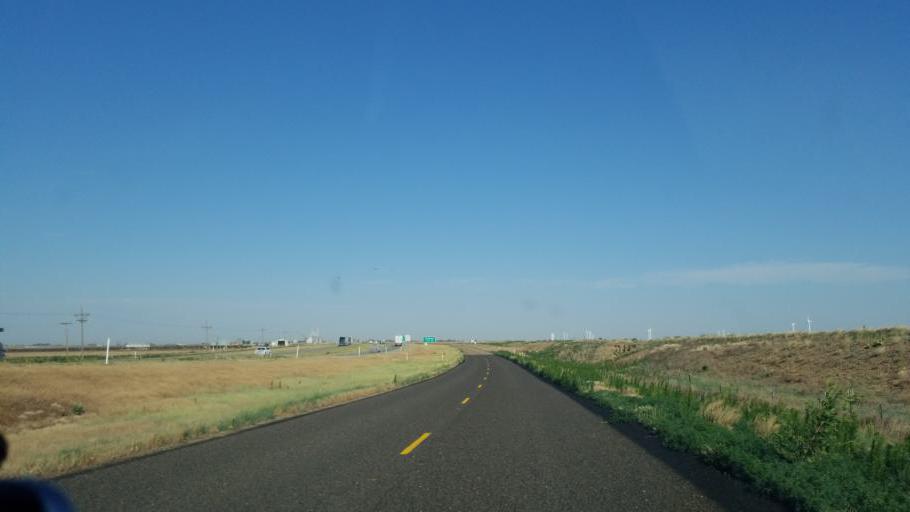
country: US
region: Texas
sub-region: Potter County
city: Bushland
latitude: 35.2080
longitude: -102.1654
